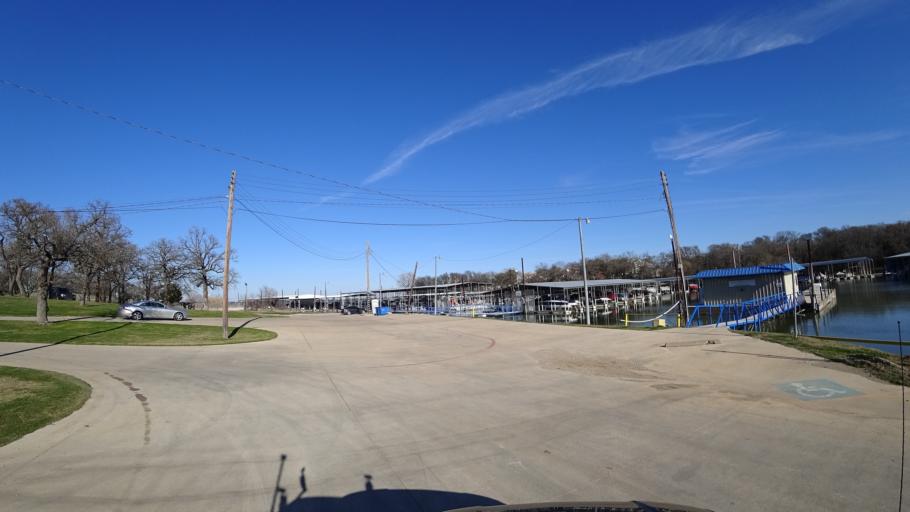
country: US
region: Texas
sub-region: Denton County
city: Highland Village
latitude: 33.0821
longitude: -97.0203
